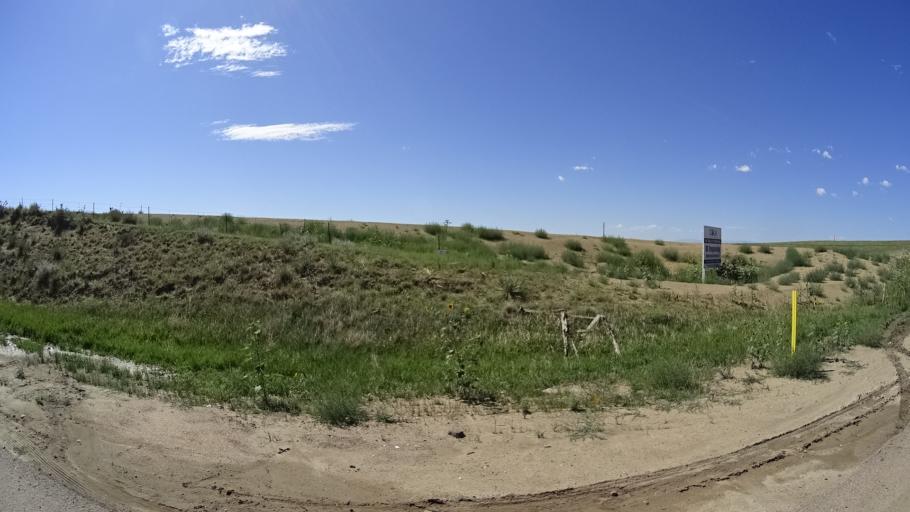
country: US
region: Colorado
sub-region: El Paso County
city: Security-Widefield
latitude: 38.7613
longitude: -104.6786
